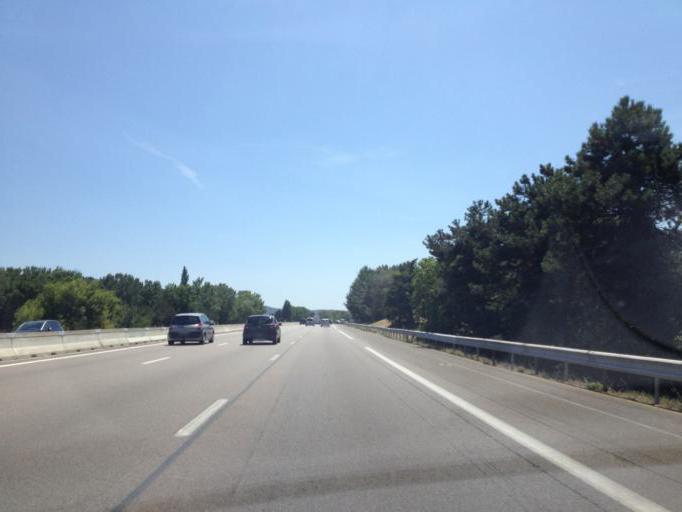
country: FR
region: Rhone-Alpes
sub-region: Departement de la Drome
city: Montboucher-sur-Jabron
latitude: 44.5599
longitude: 4.8111
